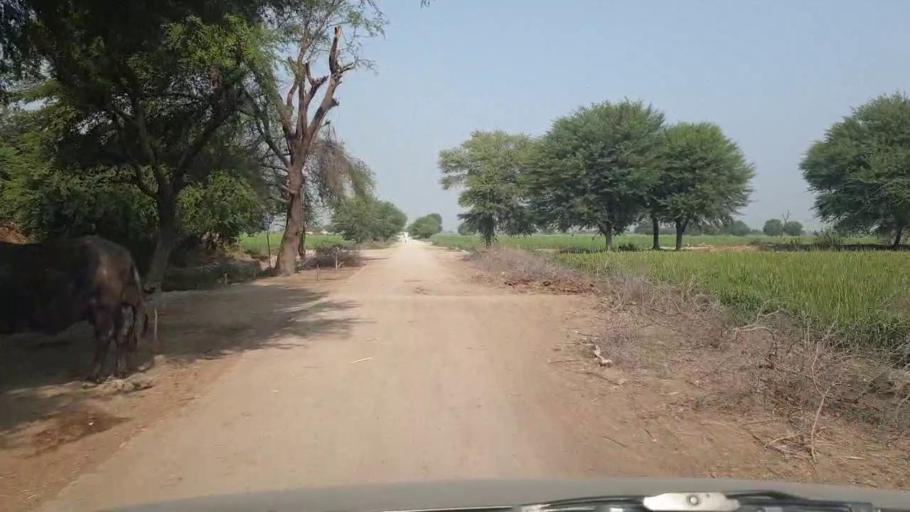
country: PK
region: Sindh
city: Umarkot
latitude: 25.4041
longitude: 69.7209
